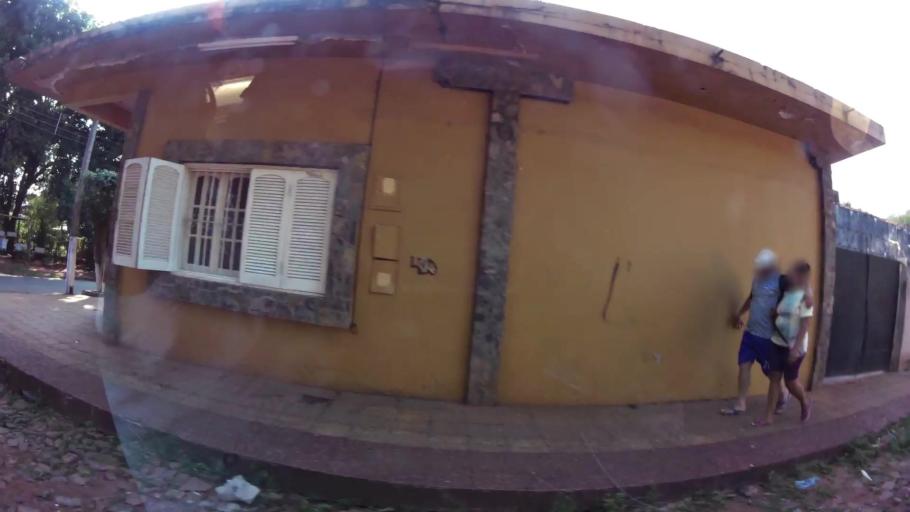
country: PY
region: Central
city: Lambare
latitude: -25.3499
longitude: -57.5896
